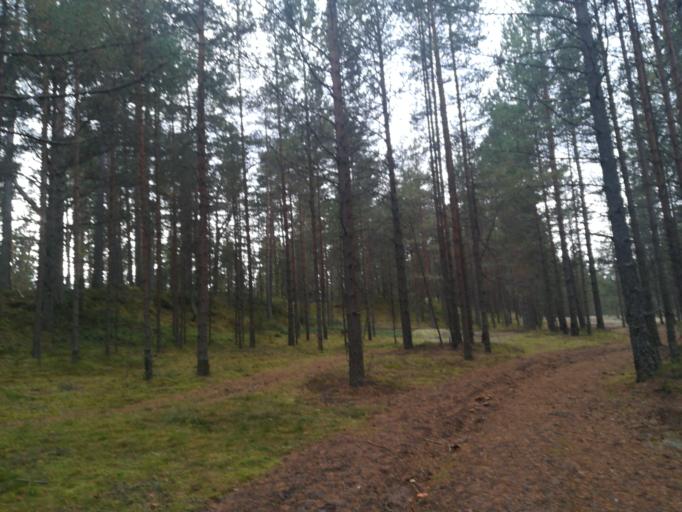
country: RU
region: Leningrad
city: Priozersk
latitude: 61.0404
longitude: 30.1888
